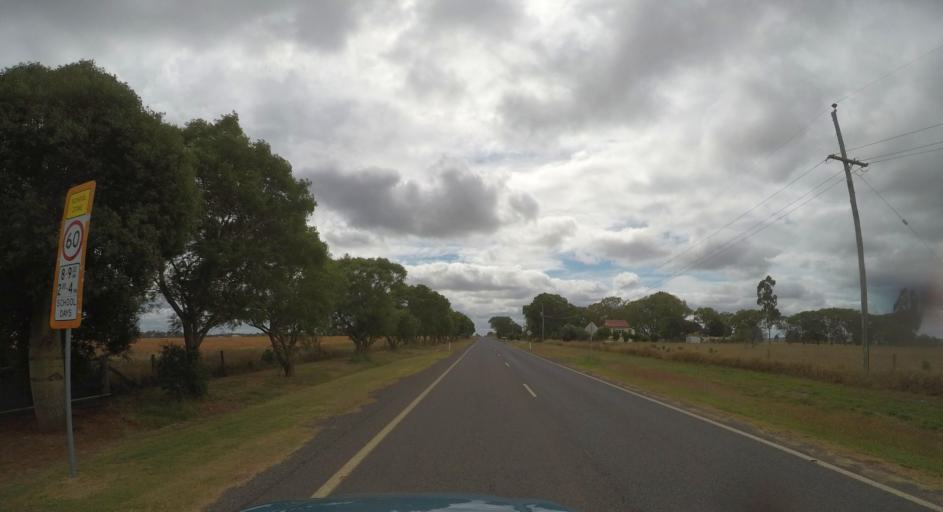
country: AU
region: Queensland
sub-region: South Burnett
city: Kingaroy
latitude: -26.3937
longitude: 151.2439
